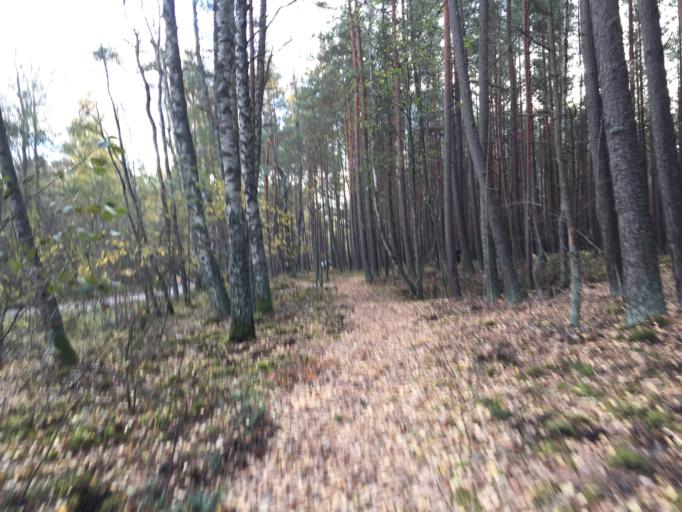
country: LV
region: Carnikava
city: Carnikava
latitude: 57.1458
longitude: 24.2636
